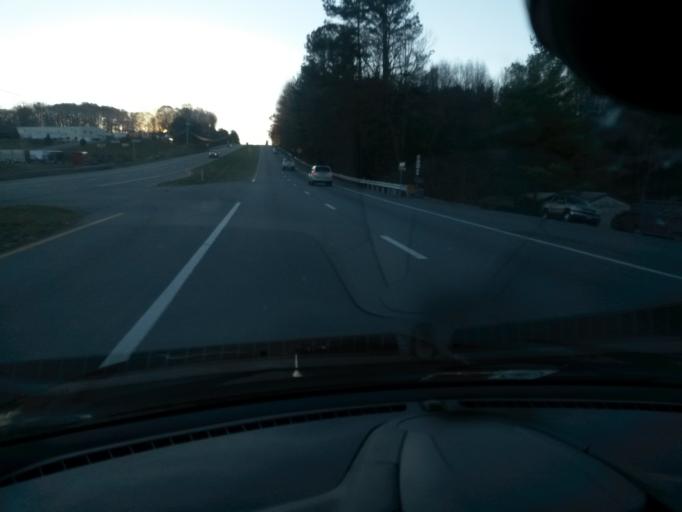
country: US
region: Virginia
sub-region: Franklin County
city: Rocky Mount
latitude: 37.0883
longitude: -79.9333
